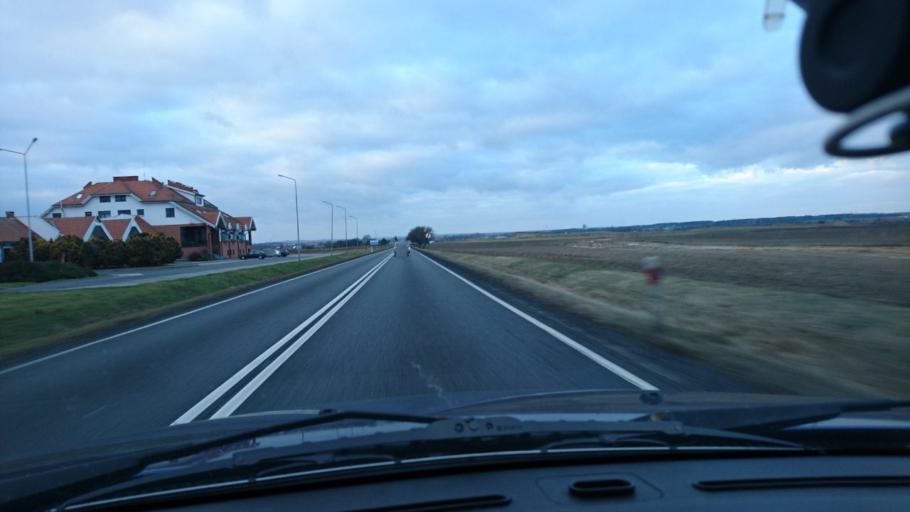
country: PL
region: Greater Poland Voivodeship
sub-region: Powiat kepinski
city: Baranow
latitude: 51.2493
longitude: 18.0161
